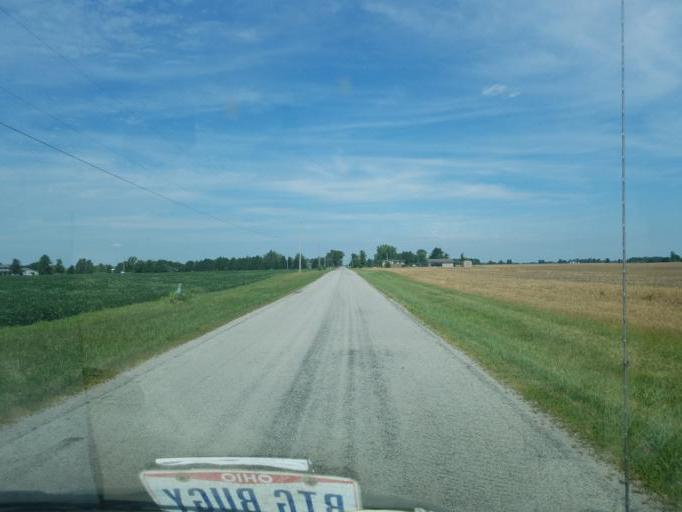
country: US
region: Ohio
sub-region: Madison County
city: West Jefferson
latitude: 39.8963
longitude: -83.3092
